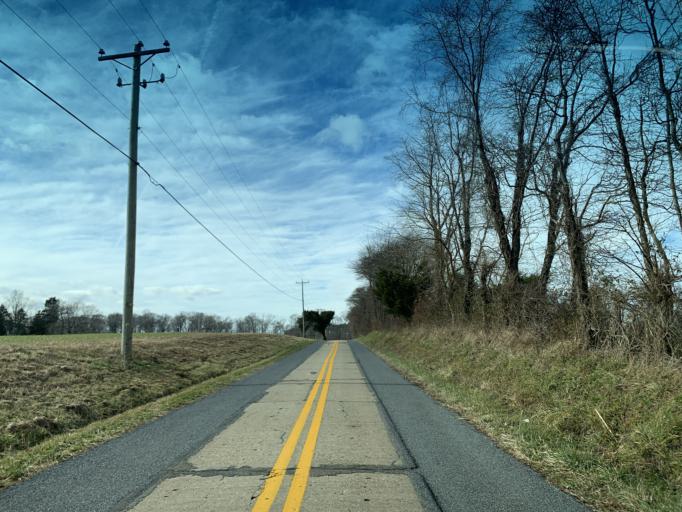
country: US
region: Maryland
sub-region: Harford County
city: Aberdeen Proving Ground
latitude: 39.3494
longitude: -76.0590
